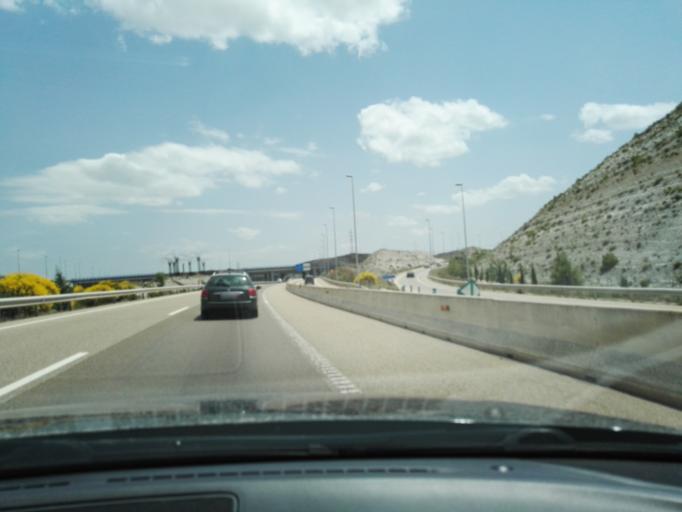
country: ES
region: Aragon
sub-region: Provincia de Zaragoza
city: Montecanal
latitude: 41.6161
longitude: -0.9359
